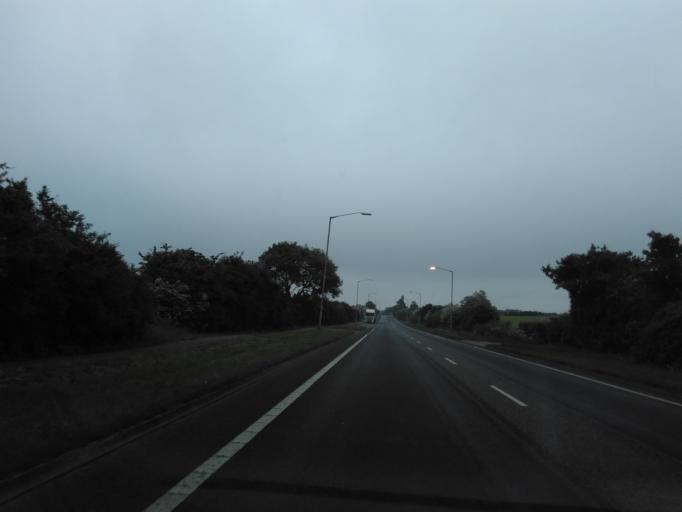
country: GB
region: England
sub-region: Kent
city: Whitstable
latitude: 51.3431
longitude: 1.0315
